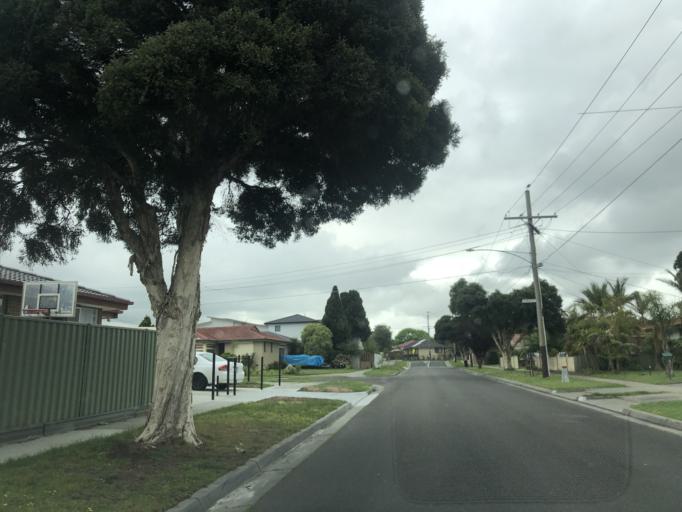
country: AU
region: Victoria
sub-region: Greater Dandenong
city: Dandenong North
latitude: -37.9615
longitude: 145.2154
